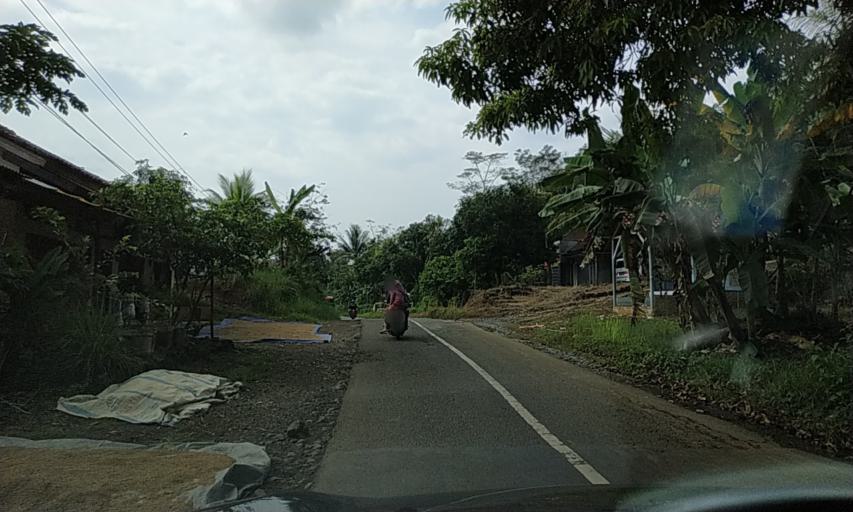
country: ID
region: Central Java
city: Meluwung
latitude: -7.3825
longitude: 108.6999
